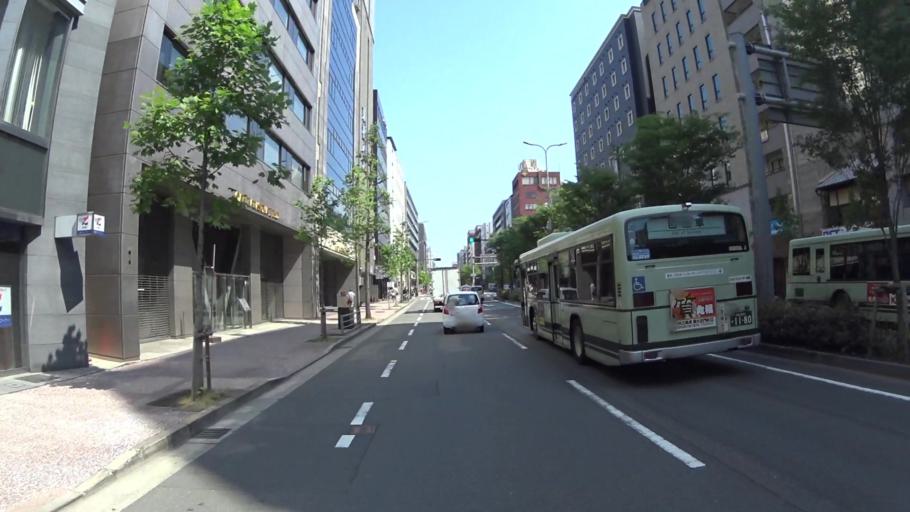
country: JP
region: Kyoto
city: Kyoto
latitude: 34.9984
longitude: 135.7590
